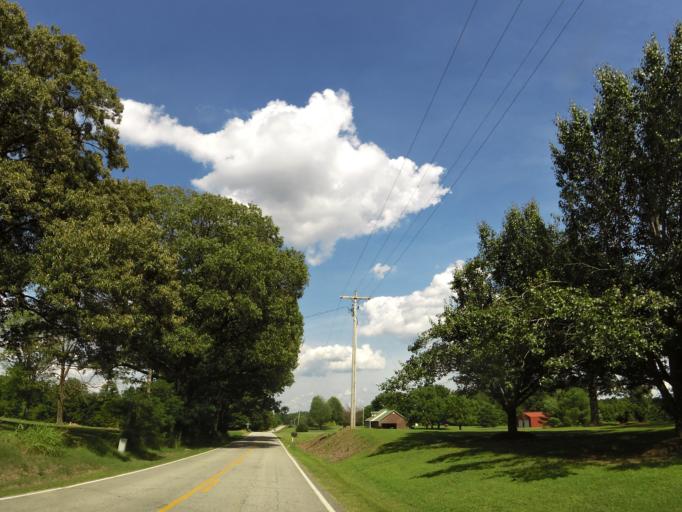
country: US
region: Tennessee
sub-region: Gibson County
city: Milan
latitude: 35.9772
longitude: -88.8227
